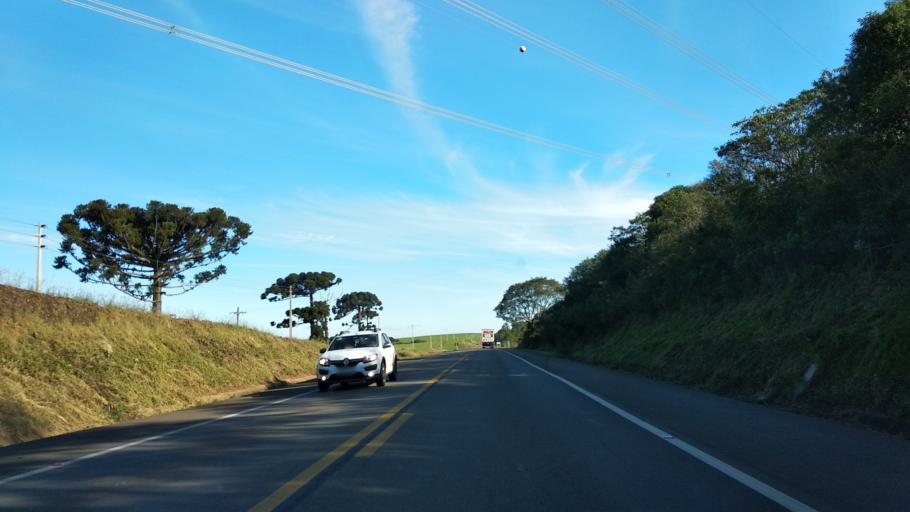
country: BR
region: Santa Catarina
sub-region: Celso Ramos
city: Celso Ramos
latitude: -27.5059
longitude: -51.3447
